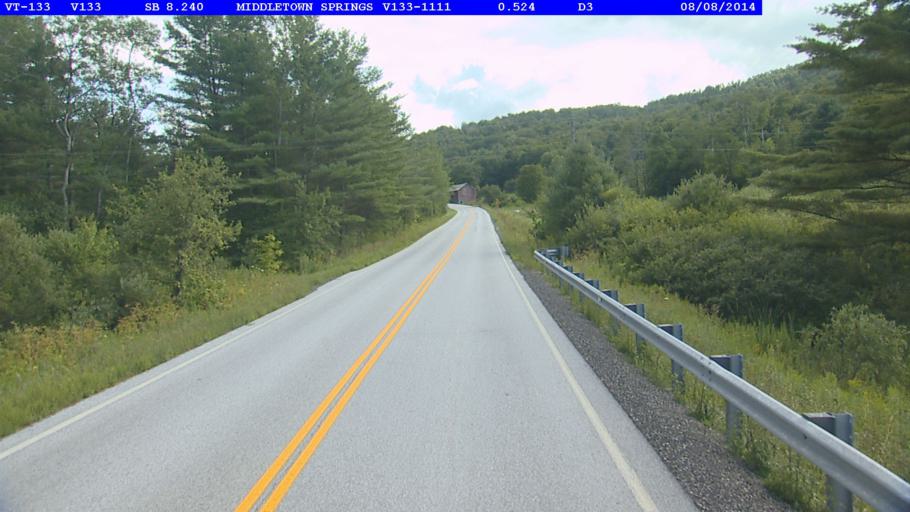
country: US
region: Vermont
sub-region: Rutland County
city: Poultney
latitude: 43.4430
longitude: -73.1114
